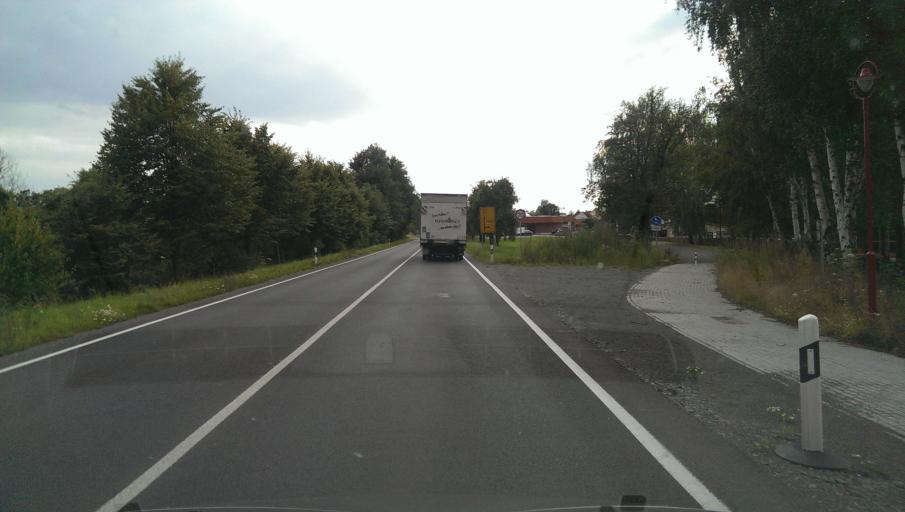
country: DE
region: Saxony
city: Groitzsch
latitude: 51.1668
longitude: 12.2698
